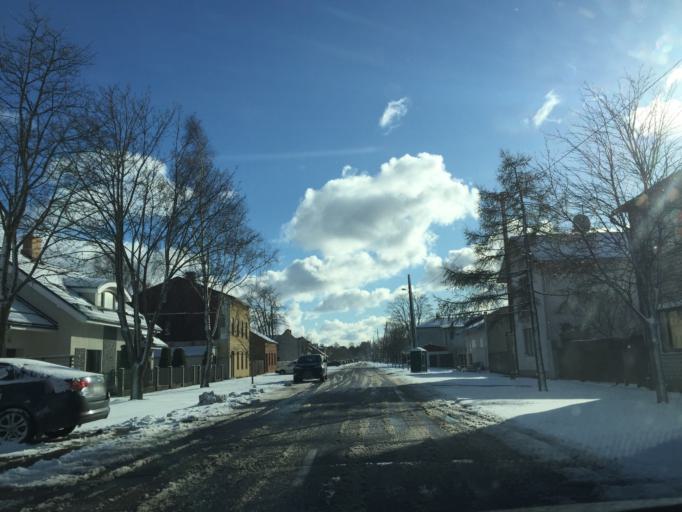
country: LV
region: Ventspils
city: Ventspils
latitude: 57.3840
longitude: 21.5568
